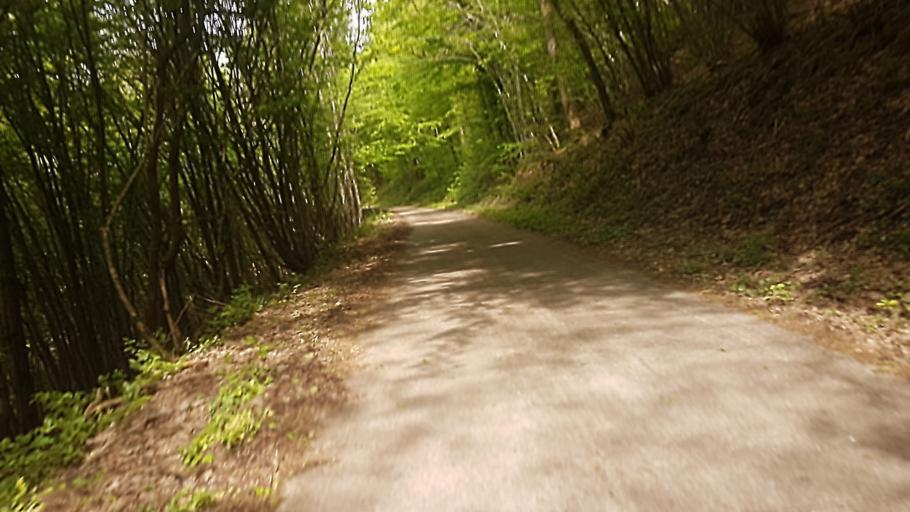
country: BE
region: Wallonia
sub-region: Province de Namur
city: Couvin
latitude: 50.0532
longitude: 4.5931
